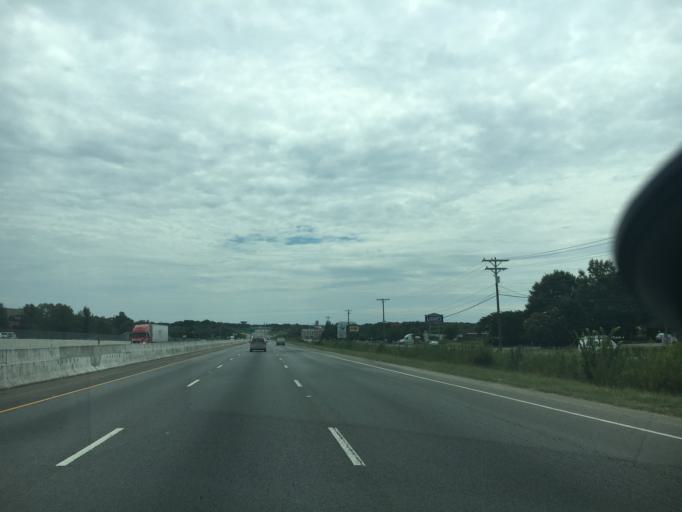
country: US
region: South Carolina
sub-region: Greenville County
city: Simpsonville
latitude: 34.7140
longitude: -82.2498
